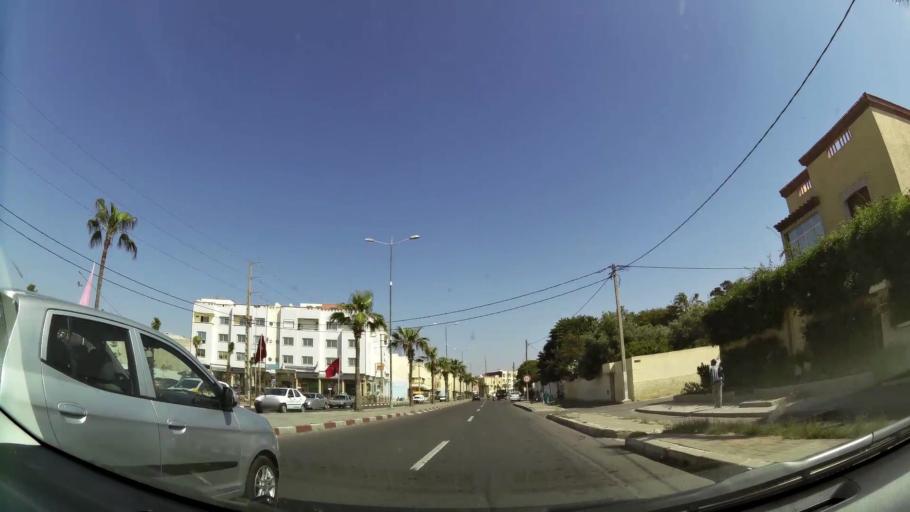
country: MA
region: Souss-Massa-Draa
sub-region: Inezgane-Ait Mellou
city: Inezgane
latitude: 30.3714
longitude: -9.5510
